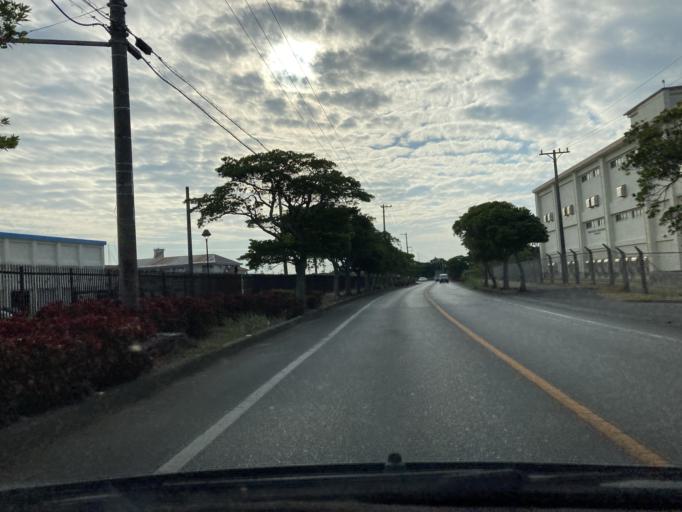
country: JP
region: Okinawa
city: Okinawa
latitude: 26.3664
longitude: 127.7996
